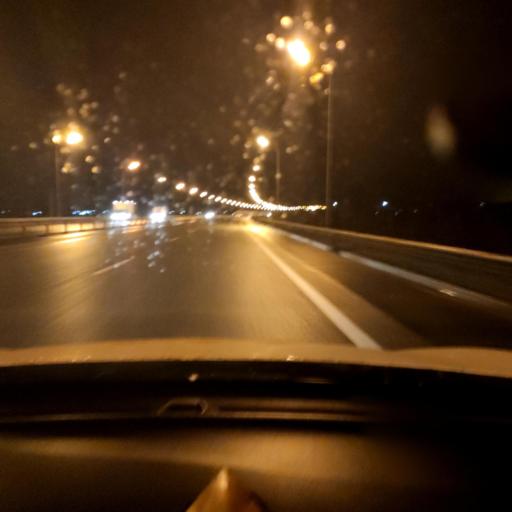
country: RU
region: Tatarstan
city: Osinovo
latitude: 55.8125
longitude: 48.8421
